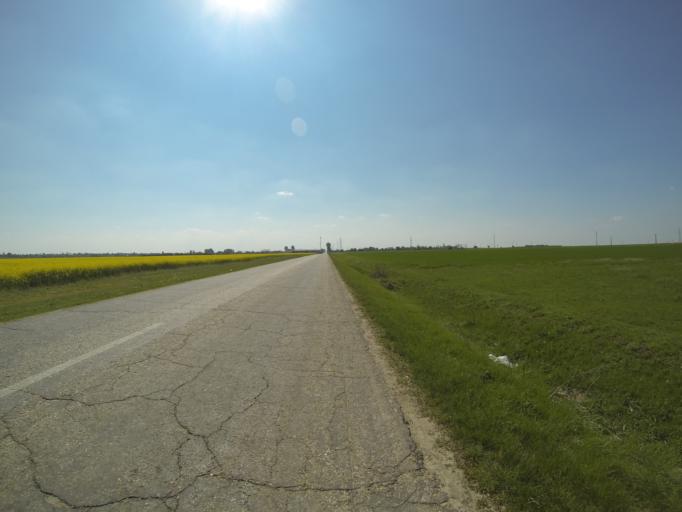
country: RO
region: Dolj
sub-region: Comuna Unirea
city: Unirea
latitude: 44.1740
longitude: 23.1909
